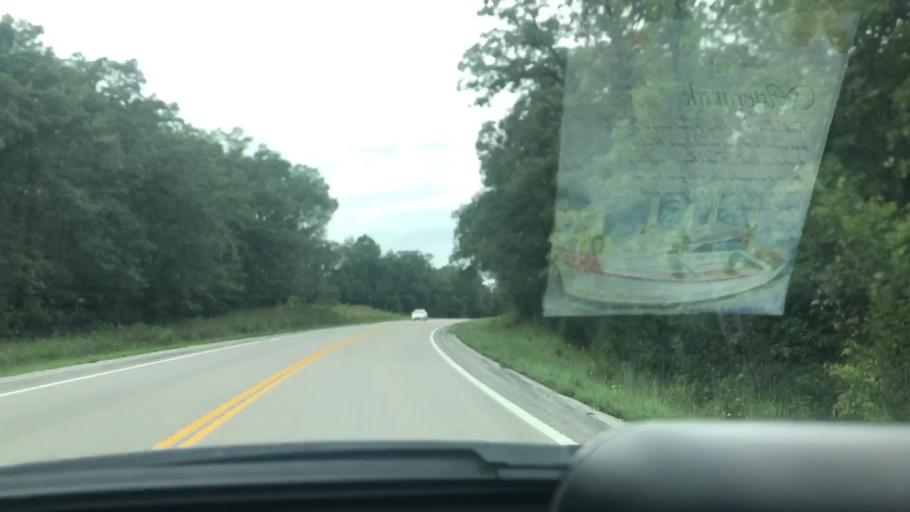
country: US
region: Missouri
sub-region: Benton County
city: Warsaw
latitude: 38.1628
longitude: -93.3035
